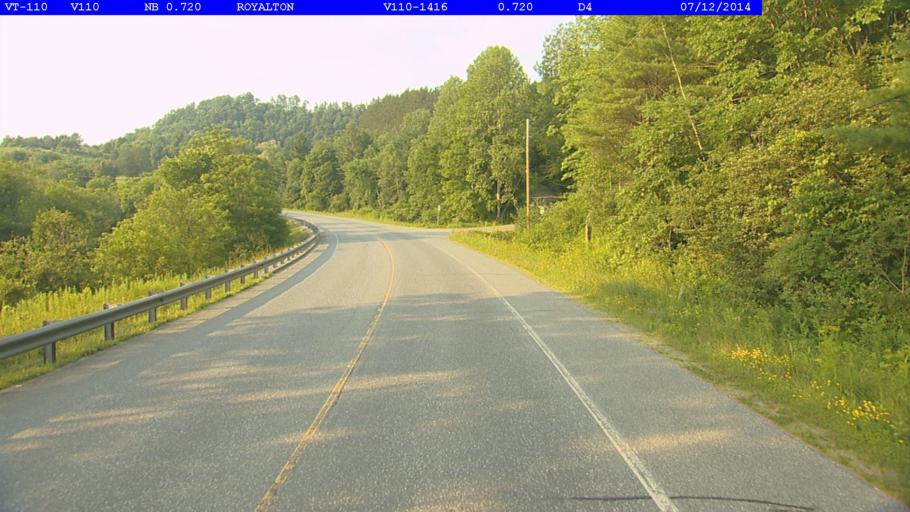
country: US
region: Vermont
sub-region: Orange County
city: Chelsea
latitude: 43.8325
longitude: -72.5120
